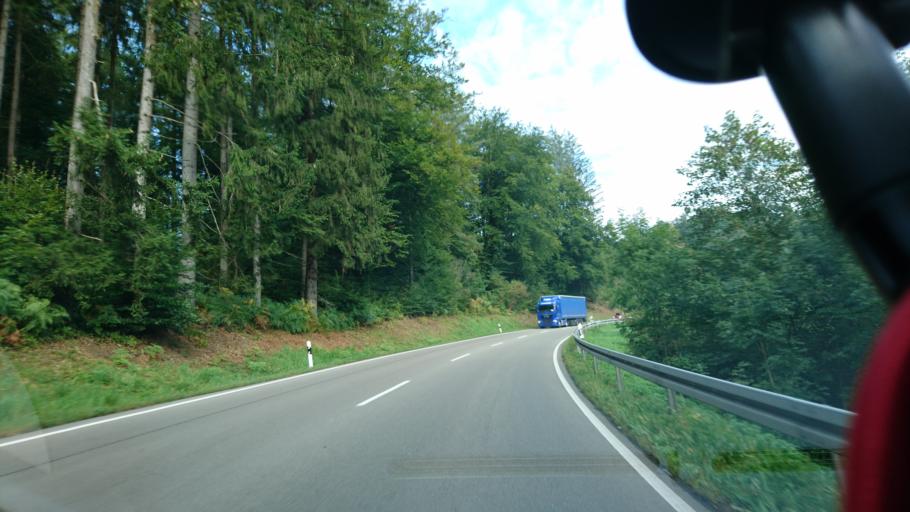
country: DE
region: Baden-Wuerttemberg
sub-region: Regierungsbezirk Stuttgart
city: Sulzbach an der Murr
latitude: 49.0200
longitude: 9.5071
